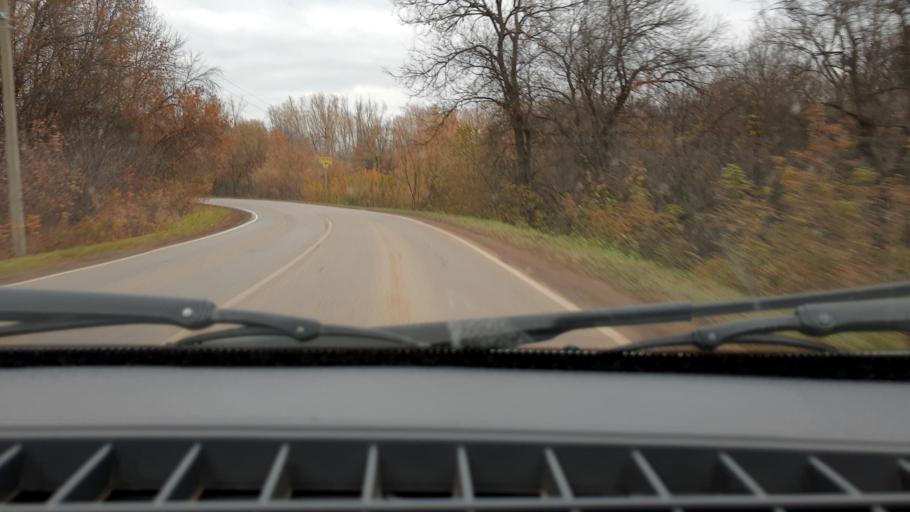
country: RU
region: Bashkortostan
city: Ufa
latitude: 54.5643
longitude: 55.9614
